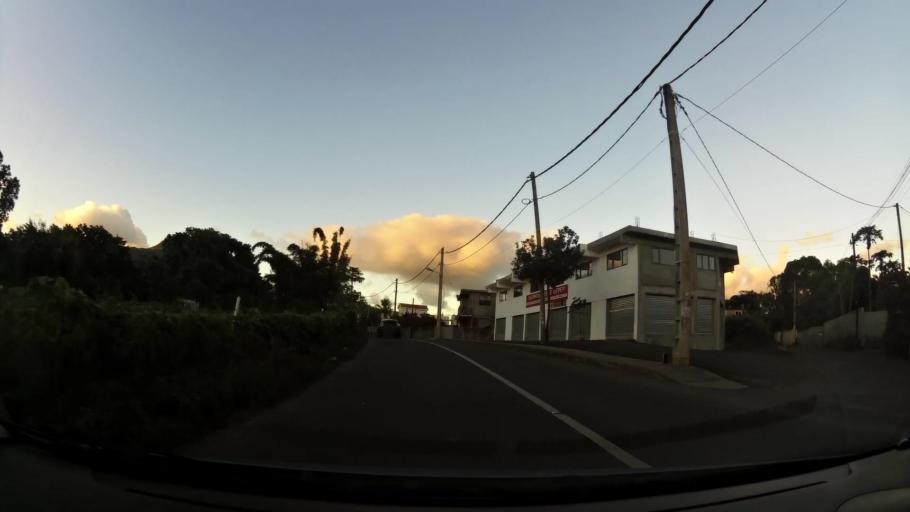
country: MU
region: Moka
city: Saint Pierre
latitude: -20.2191
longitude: 57.5175
